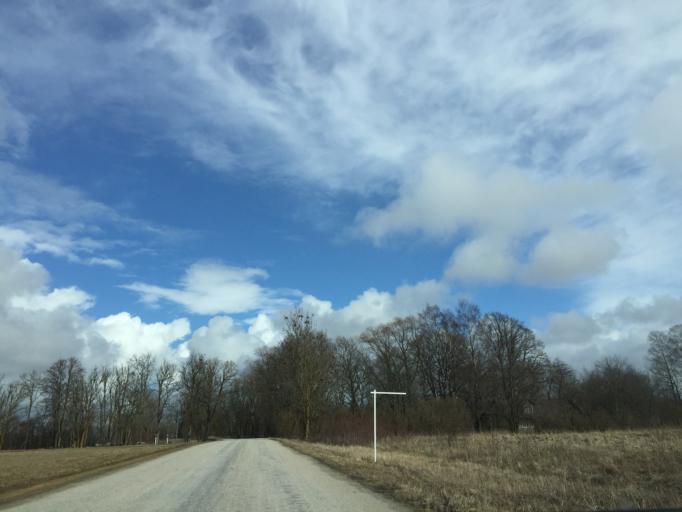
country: EE
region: Laeaene
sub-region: Lihula vald
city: Lihula
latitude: 58.7352
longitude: 23.8287
